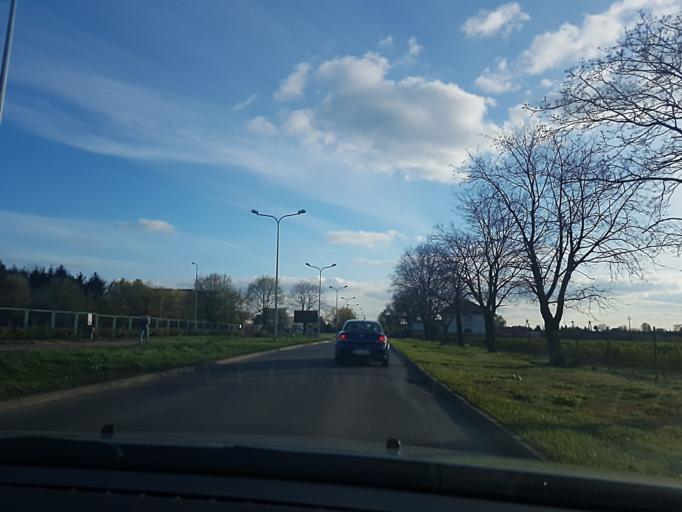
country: PL
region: Lodz Voivodeship
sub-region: Powiat kutnowski
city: Kutno
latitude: 52.2422
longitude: 19.3739
